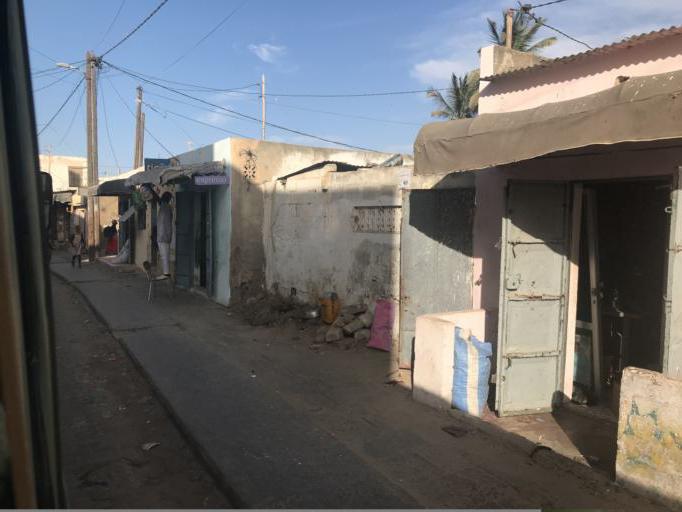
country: SN
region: Saint-Louis
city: Saint-Louis
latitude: 16.0069
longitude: -16.4947
